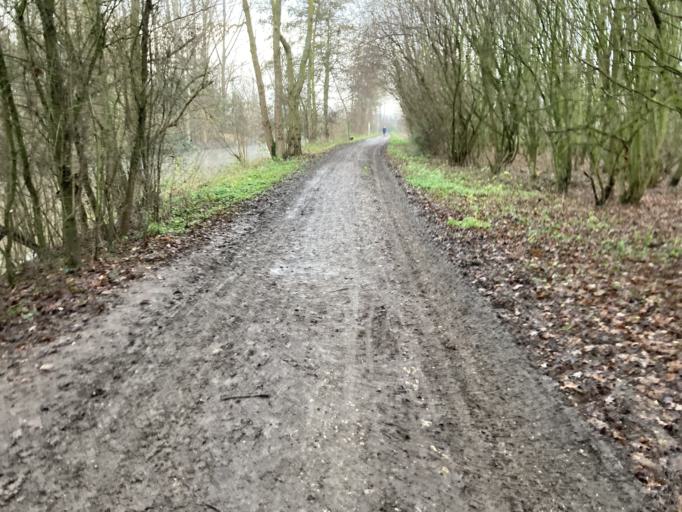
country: DE
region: North Rhine-Westphalia
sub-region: Regierungsbezirk Dusseldorf
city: Neubrueck
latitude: 51.1220
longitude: 6.6344
